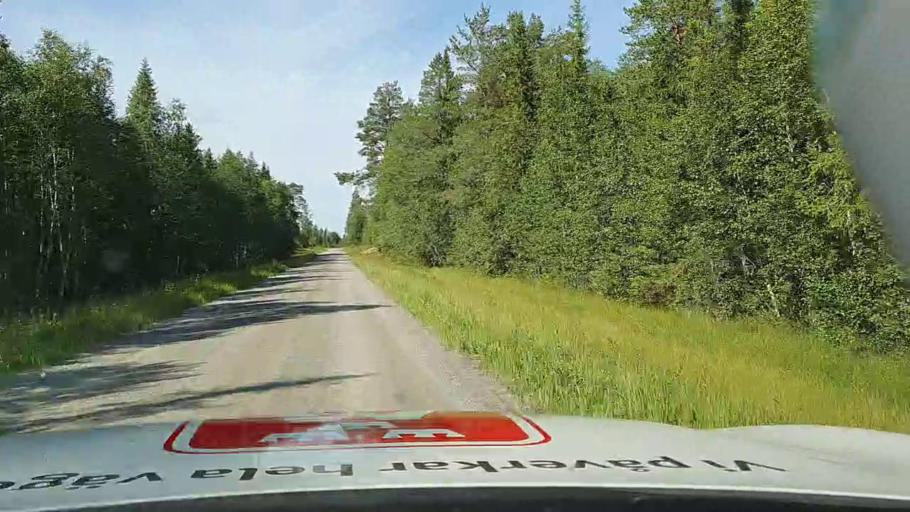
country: SE
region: Jaemtland
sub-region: Stroemsunds Kommun
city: Stroemsund
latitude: 63.7105
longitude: 15.3097
